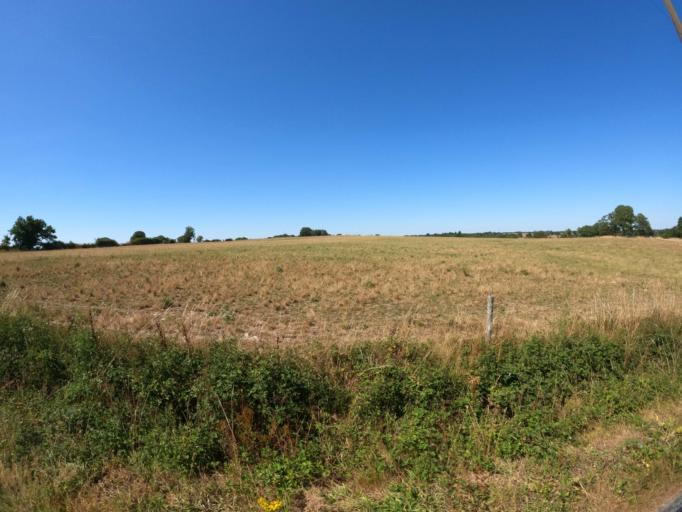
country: FR
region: Pays de la Loire
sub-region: Departement de la Vendee
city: Saint-Aubin-des-Ormeaux
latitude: 46.9984
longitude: -1.0277
